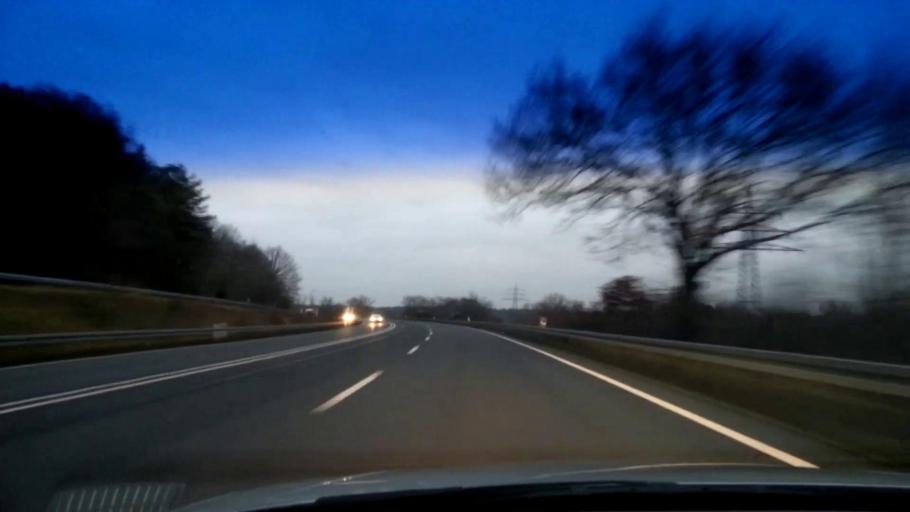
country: DE
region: Bavaria
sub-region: Upper Franconia
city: Hirschaid
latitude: 49.8132
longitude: 10.9647
